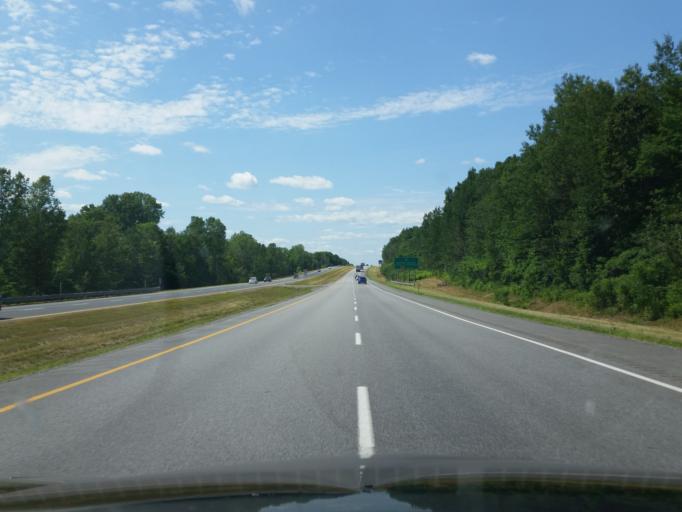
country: CA
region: Quebec
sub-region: Monteregie
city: Hudson
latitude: 45.4477
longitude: -74.2058
